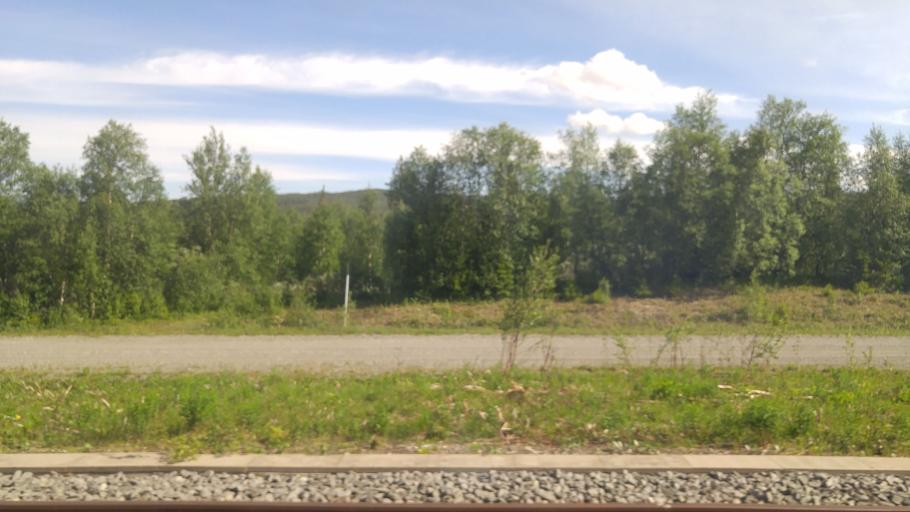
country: NO
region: Nord-Trondelag
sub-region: Meraker
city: Meraker
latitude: 63.2891
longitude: 12.3414
